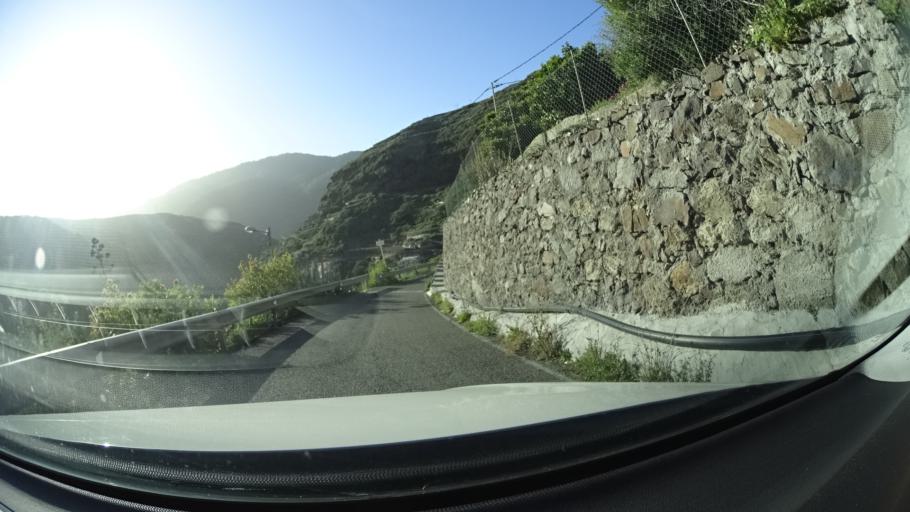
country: ES
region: Canary Islands
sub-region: Provincia de Las Palmas
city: Artenara
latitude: 28.0453
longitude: -15.6591
